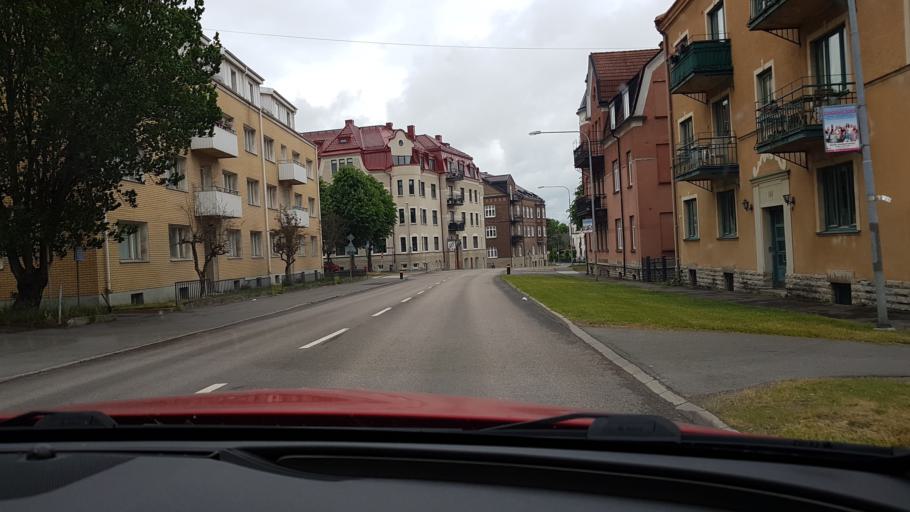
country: SE
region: Vaestra Goetaland
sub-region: Skovde Kommun
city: Skoevde
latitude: 58.3831
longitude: 13.8435
